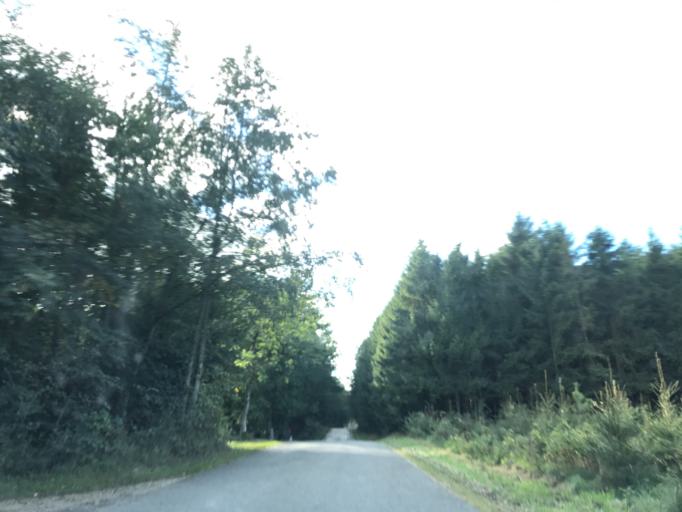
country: DK
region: Central Jutland
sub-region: Silkeborg Kommune
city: Kjellerup
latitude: 56.2583
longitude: 9.4863
